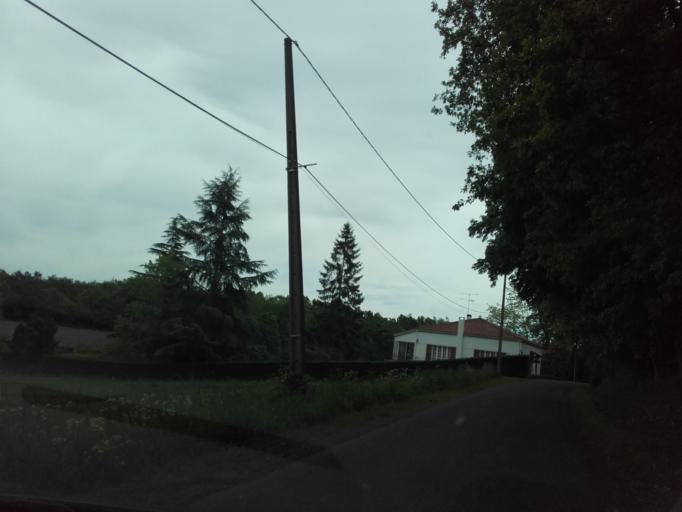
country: FR
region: Aquitaine
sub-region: Departement de la Dordogne
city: Monbazillac
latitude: 44.7761
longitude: 0.4517
